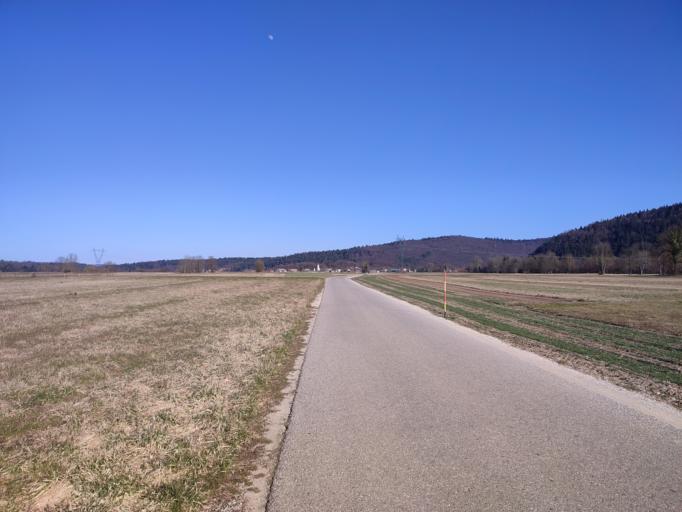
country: SI
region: Ig
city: Ig
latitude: 45.9432
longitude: 14.4911
